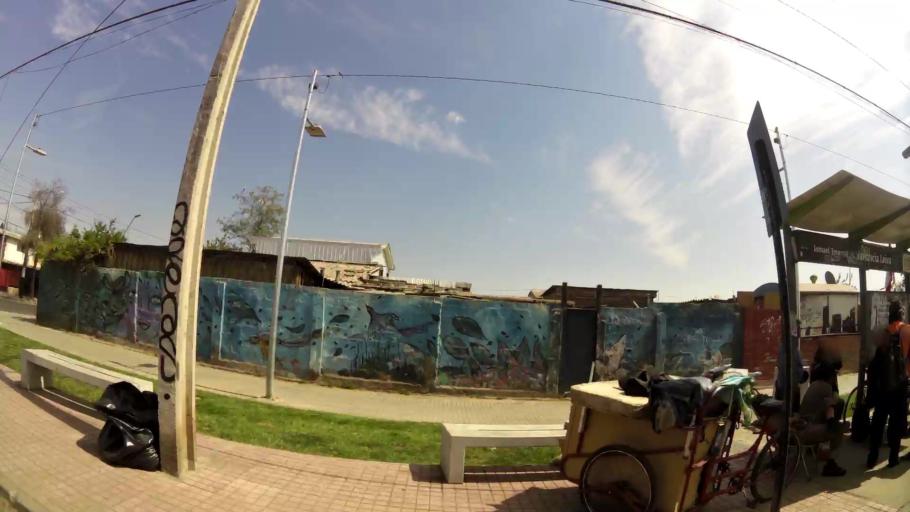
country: CL
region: Santiago Metropolitan
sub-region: Provincia de Santiago
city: La Pintana
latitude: -33.5552
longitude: -70.6519
